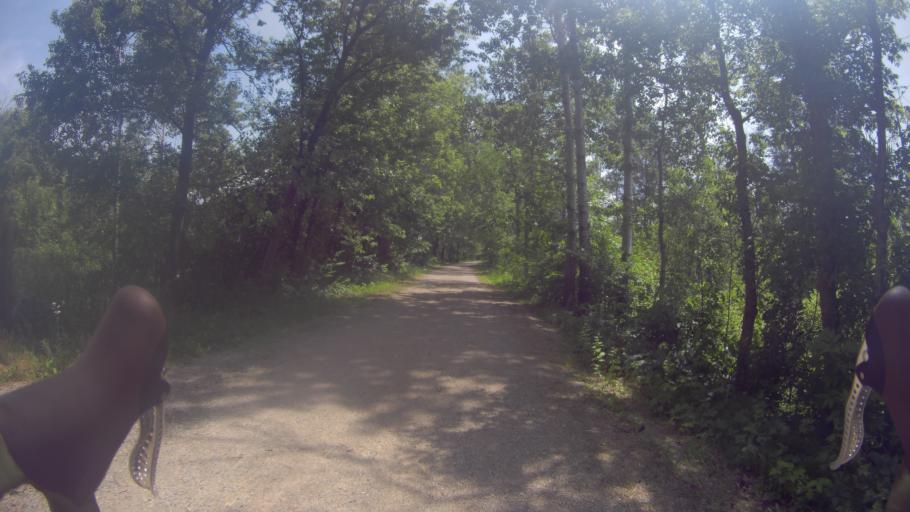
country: US
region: Wisconsin
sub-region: Jefferson County
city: Lake Mills
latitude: 43.0683
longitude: -88.9429
